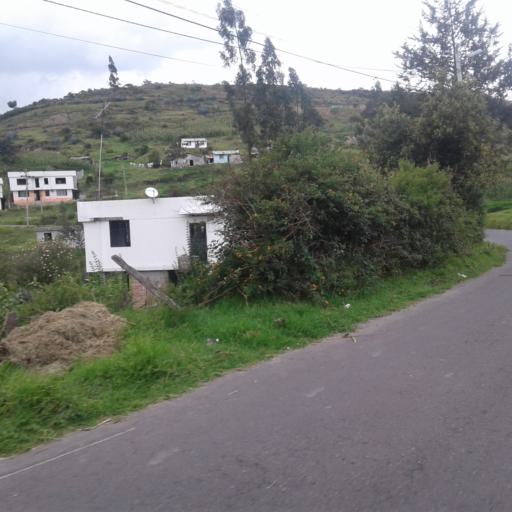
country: EC
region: Pichincha
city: Sangolqui
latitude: -0.2918
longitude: -78.3884
